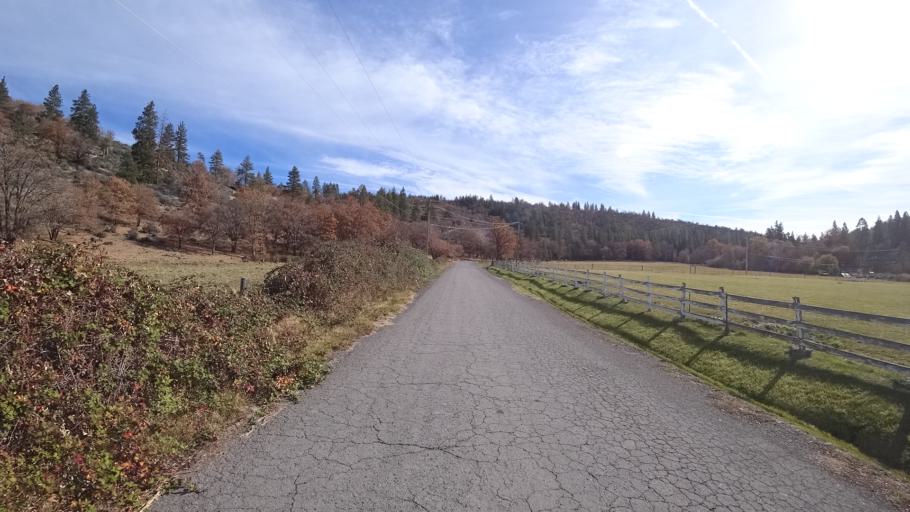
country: US
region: California
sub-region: Siskiyou County
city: Weed
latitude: 41.4466
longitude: -122.4271
